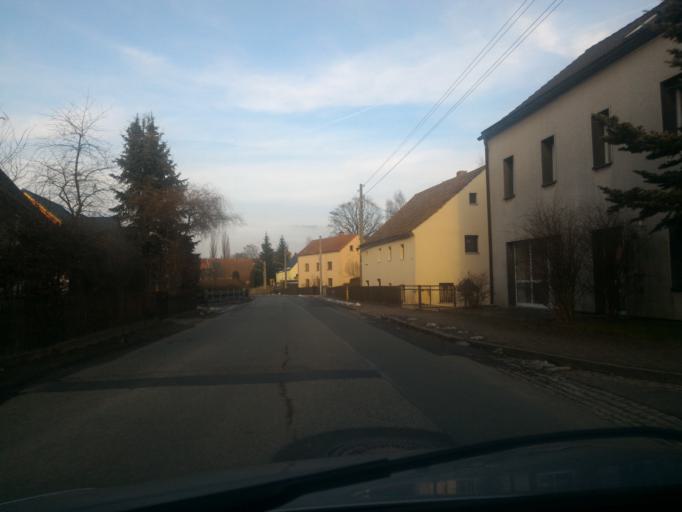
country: DE
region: Saxony
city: Olbersdorf
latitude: 50.8792
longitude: 14.7763
